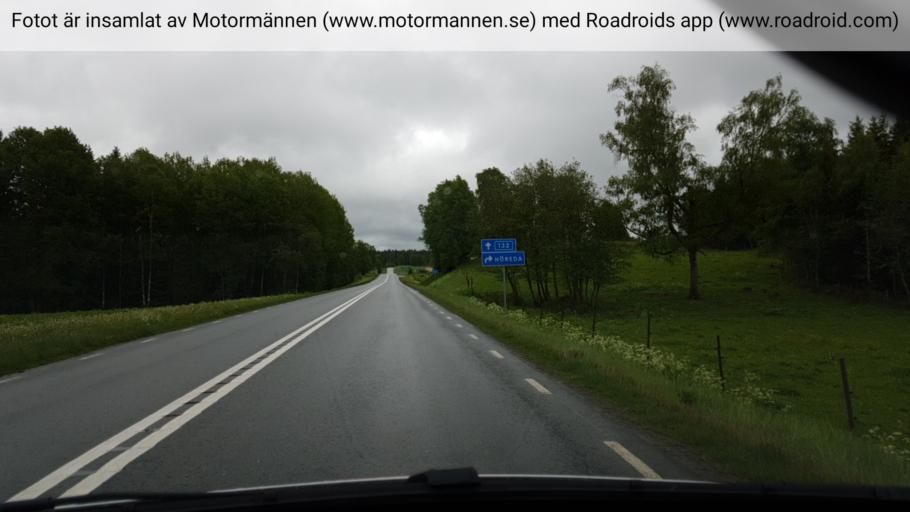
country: SE
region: Joenkoeping
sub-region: Jonkopings Kommun
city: Tenhult
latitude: 57.7763
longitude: 14.4619
